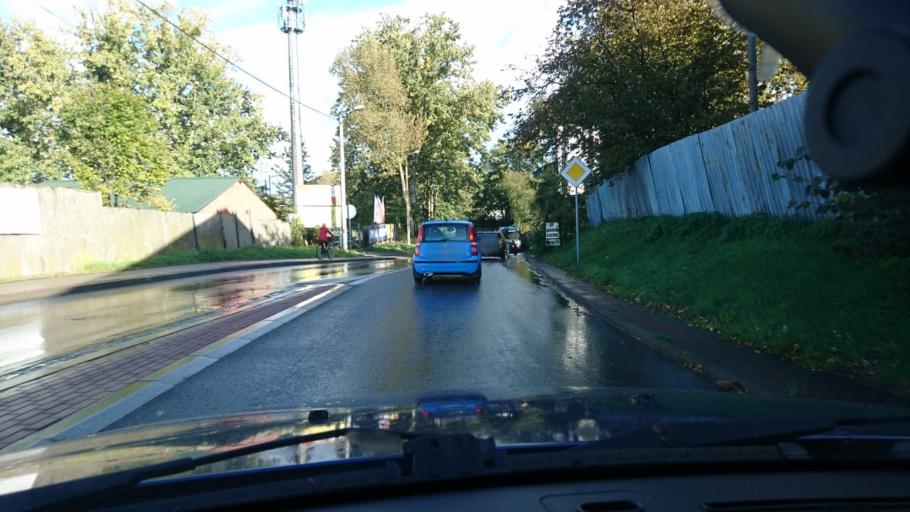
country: PL
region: Silesian Voivodeship
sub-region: Bielsko-Biala
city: Bielsko-Biala
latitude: 49.8553
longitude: 19.0360
